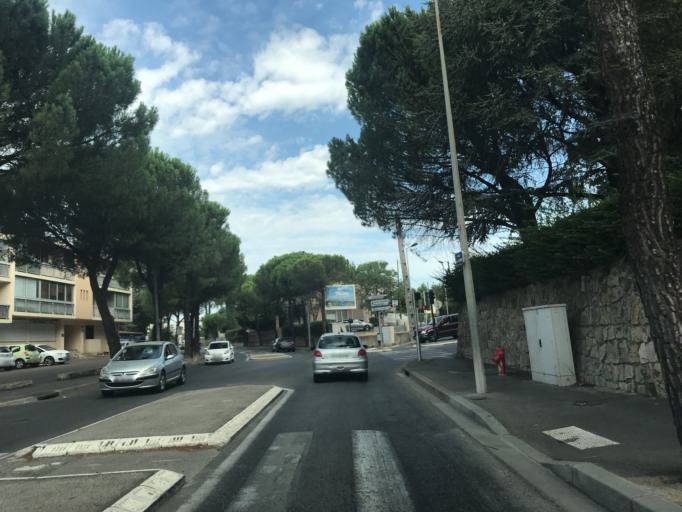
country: FR
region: Provence-Alpes-Cote d'Azur
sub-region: Departement des Bouches-du-Rhone
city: Aix-en-Provence
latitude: 43.5172
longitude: 5.4354
